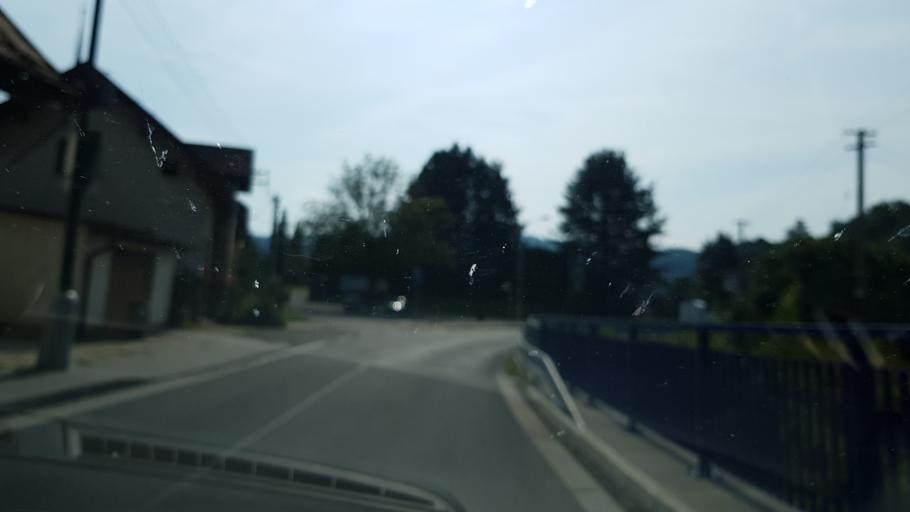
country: CZ
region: Olomoucky
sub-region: Okres Jesenik
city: Jesenik
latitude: 50.2193
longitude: 17.2095
